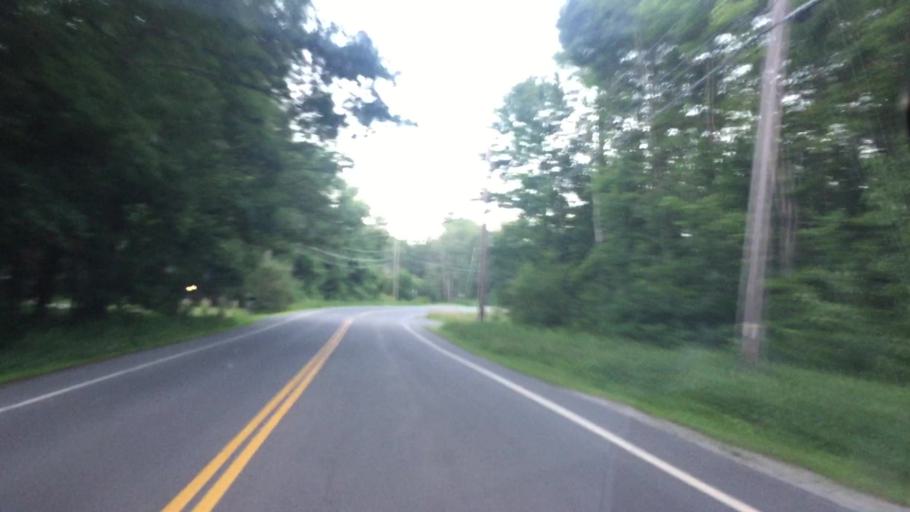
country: US
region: Massachusetts
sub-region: Middlesex County
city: Tyngsboro
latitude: 42.7023
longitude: -71.3819
